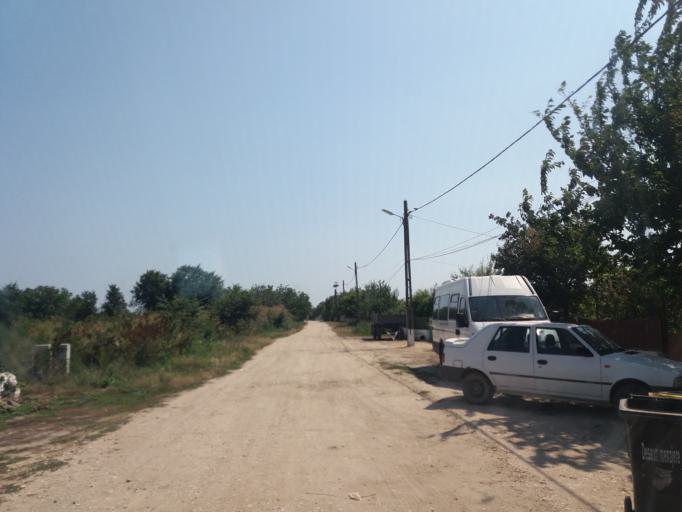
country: RO
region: Constanta
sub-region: Comuna Sacele
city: Sacele
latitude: 44.4561
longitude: 28.7382
